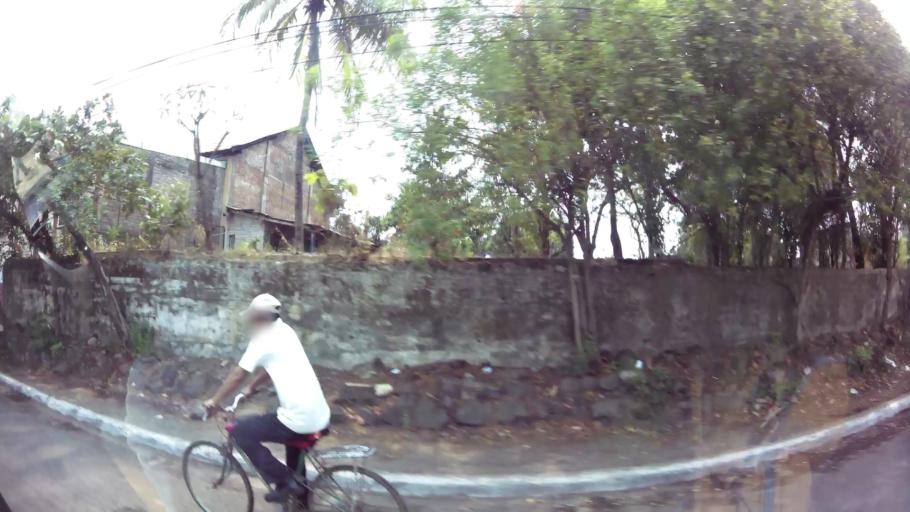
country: NI
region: Chinandega
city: Chinandega
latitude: 12.6361
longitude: -87.1320
